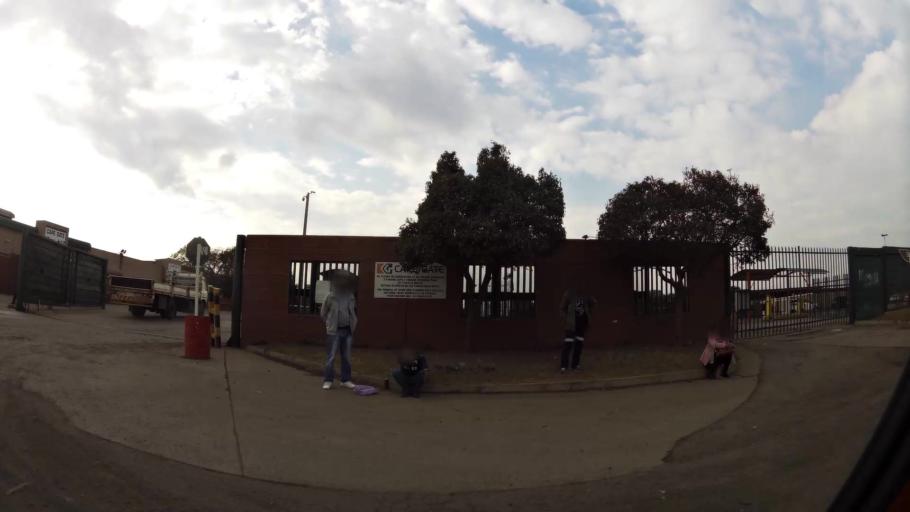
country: ZA
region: Gauteng
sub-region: Sedibeng District Municipality
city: Vanderbijlpark
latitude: -26.6640
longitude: 27.8568
